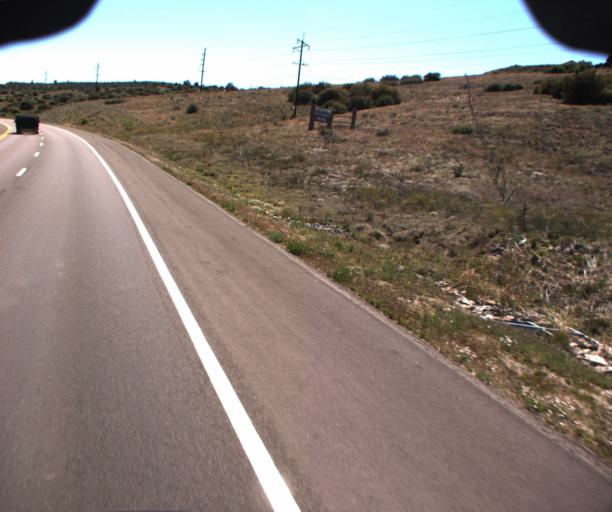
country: US
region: Arizona
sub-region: Yavapai County
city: Prescott
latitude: 34.5708
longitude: -112.4388
